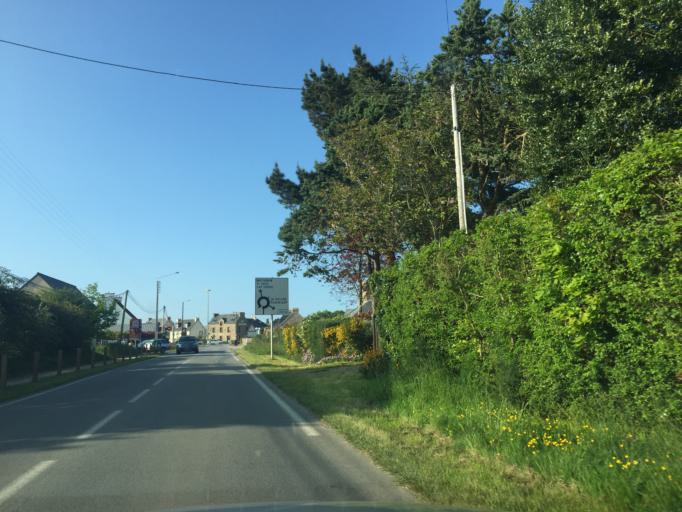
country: FR
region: Brittany
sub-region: Departement des Cotes-d'Armor
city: Crehen
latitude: 48.5810
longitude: -2.2346
